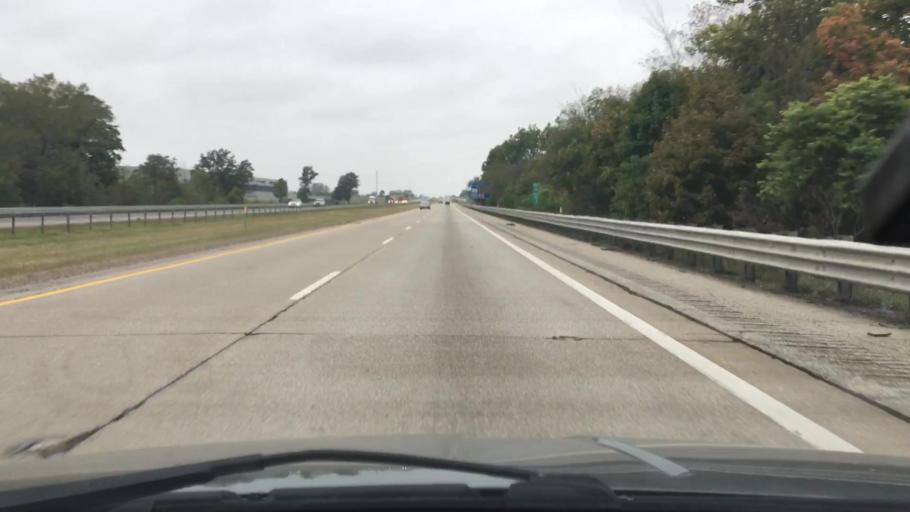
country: US
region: Michigan
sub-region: Berrien County
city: Watervliet
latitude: 42.1791
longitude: -86.2492
